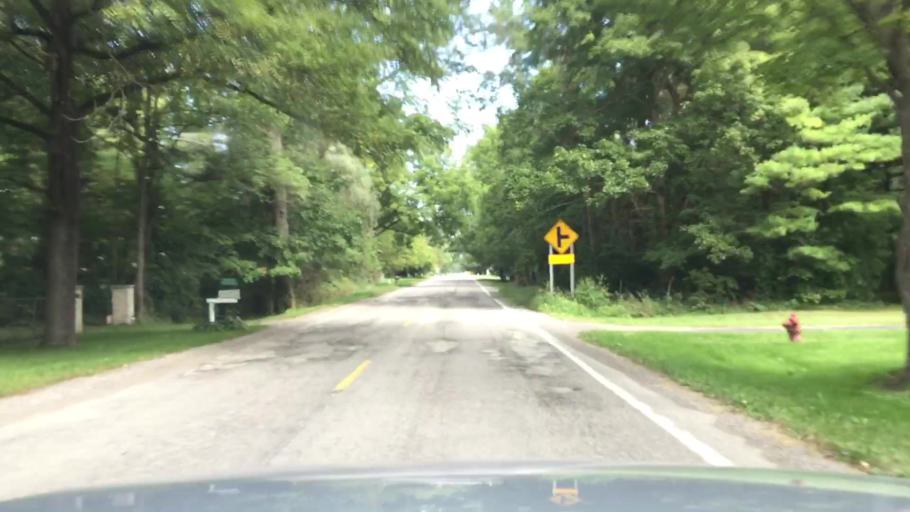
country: US
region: Michigan
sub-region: Wayne County
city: Belleville
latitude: 42.1545
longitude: -83.4612
